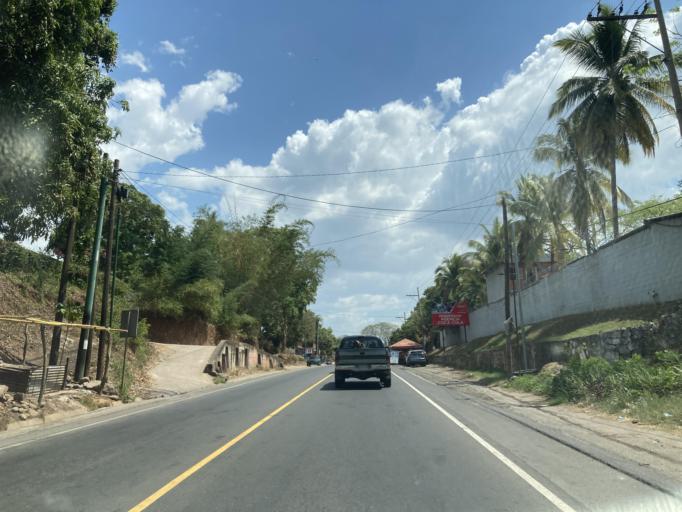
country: GT
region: Santa Rosa
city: Guazacapan
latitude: 14.0669
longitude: -90.4051
